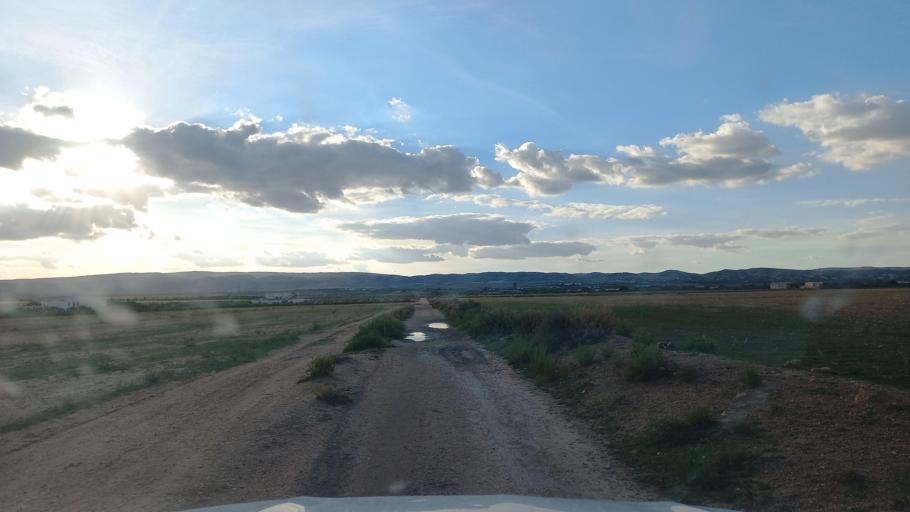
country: TN
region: Al Qasrayn
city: Sbiba
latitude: 35.3508
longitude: 9.0398
